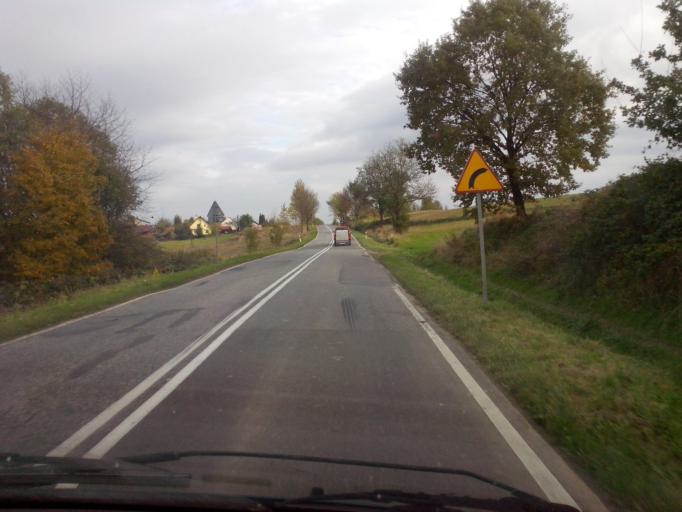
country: PL
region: Subcarpathian Voivodeship
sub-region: Powiat strzyzowski
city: Wisniowa
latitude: 49.8744
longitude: 21.6535
